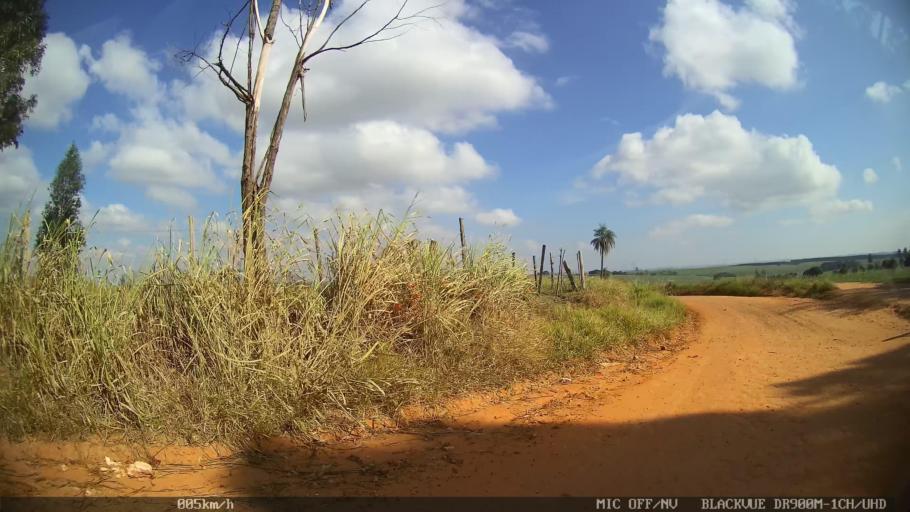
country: BR
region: Sao Paulo
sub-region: Indaiatuba
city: Indaiatuba
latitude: -22.9941
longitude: -47.2110
